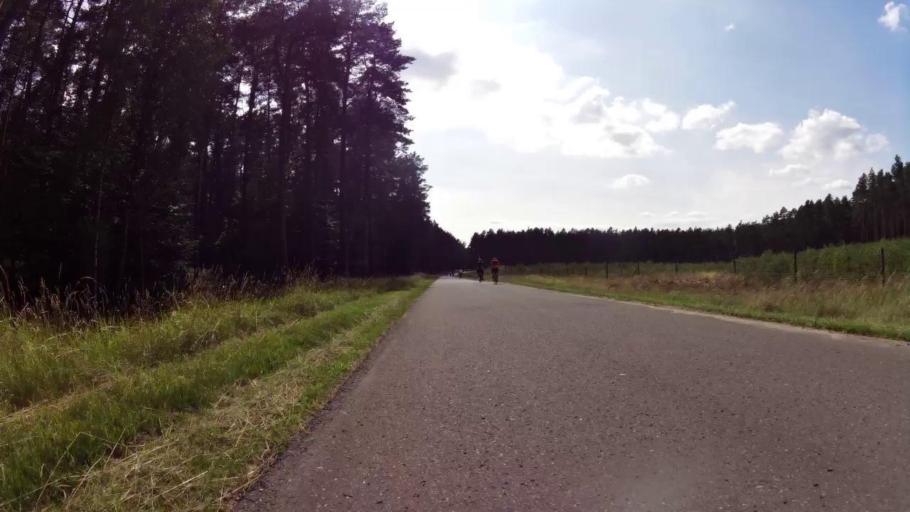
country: PL
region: West Pomeranian Voivodeship
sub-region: Powiat choszczenski
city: Drawno
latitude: 53.3676
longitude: 15.7192
